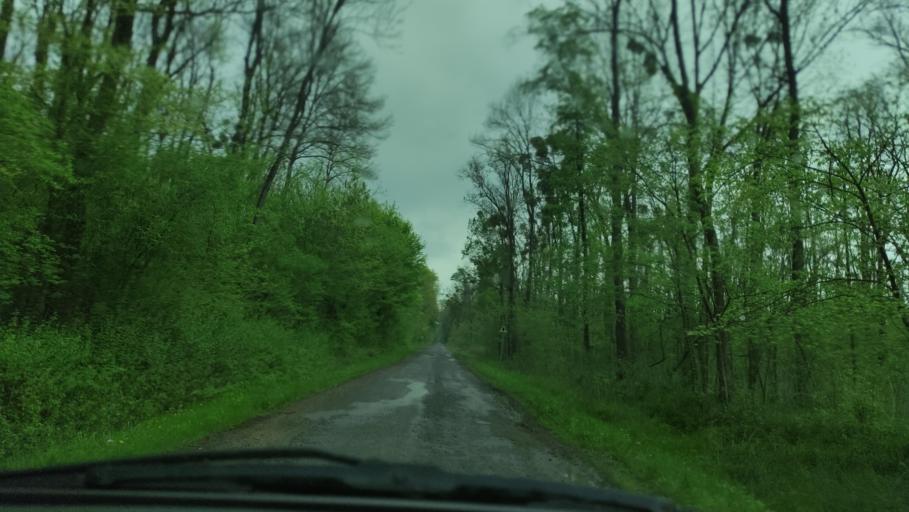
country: HU
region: Baranya
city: Mohacs
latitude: 45.9217
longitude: 18.7284
